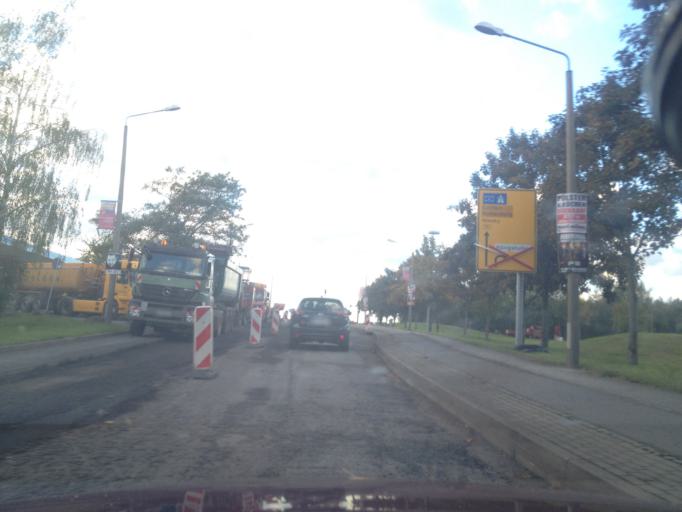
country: DE
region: Saxony
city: Goerlitz
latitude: 51.1633
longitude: 14.9735
